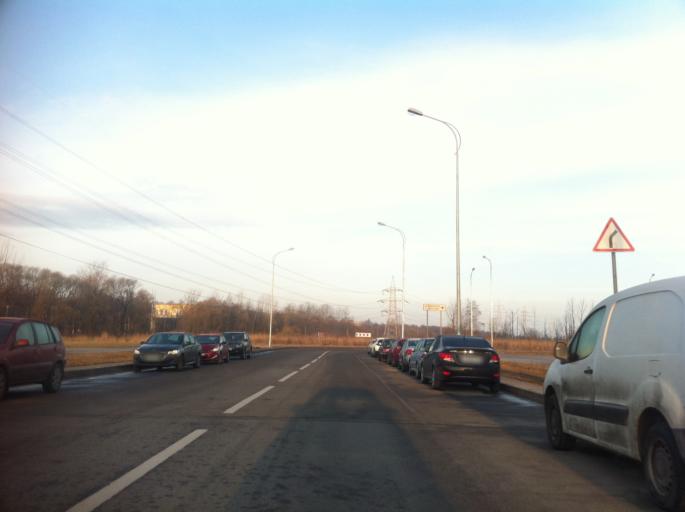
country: RU
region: St.-Petersburg
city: Sosnovaya Polyana
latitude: 59.8481
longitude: 30.1349
